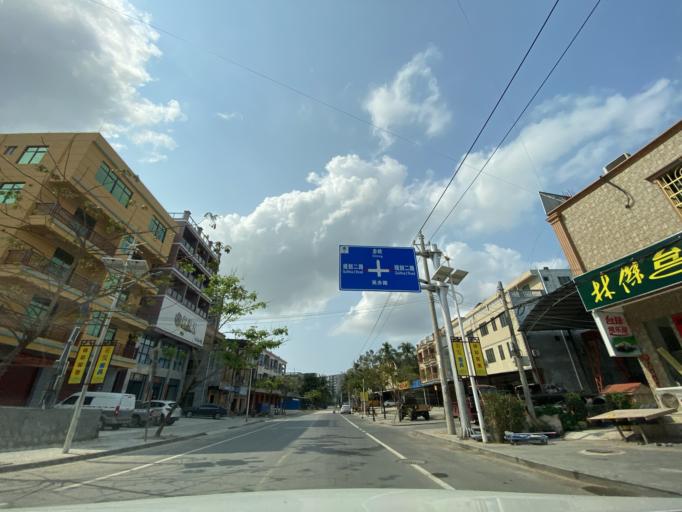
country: CN
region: Hainan
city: Yingzhou
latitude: 18.4197
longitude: 109.8497
